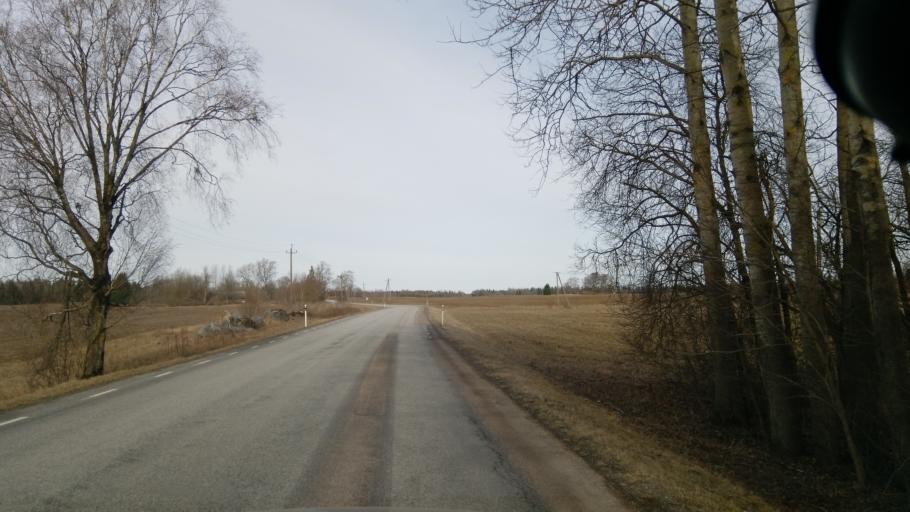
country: EE
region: Raplamaa
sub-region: Rapla vald
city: Rapla
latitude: 59.0267
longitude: 24.8383
